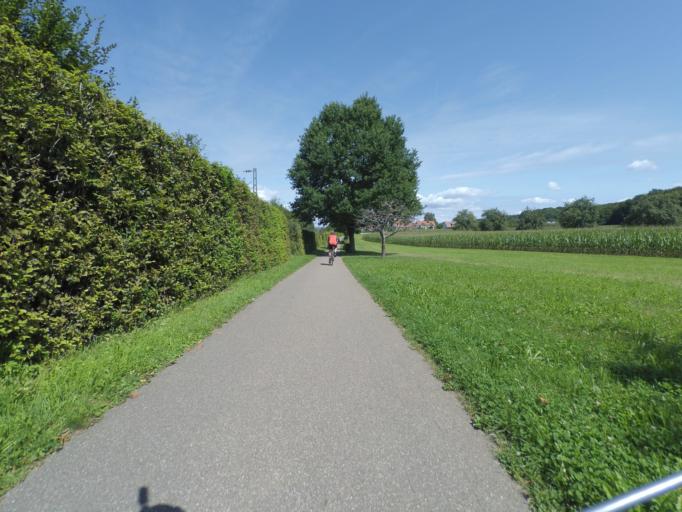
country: DE
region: Baden-Wuerttemberg
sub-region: Freiburg Region
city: Gundelfingen
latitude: 48.0388
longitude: 7.8720
